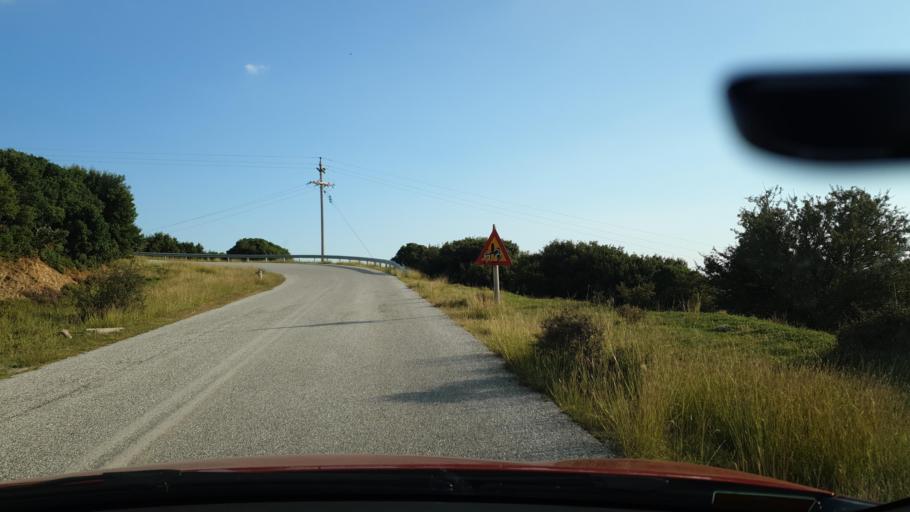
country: GR
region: Central Macedonia
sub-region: Nomos Thessalonikis
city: Peristera
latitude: 40.5253
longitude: 23.1906
